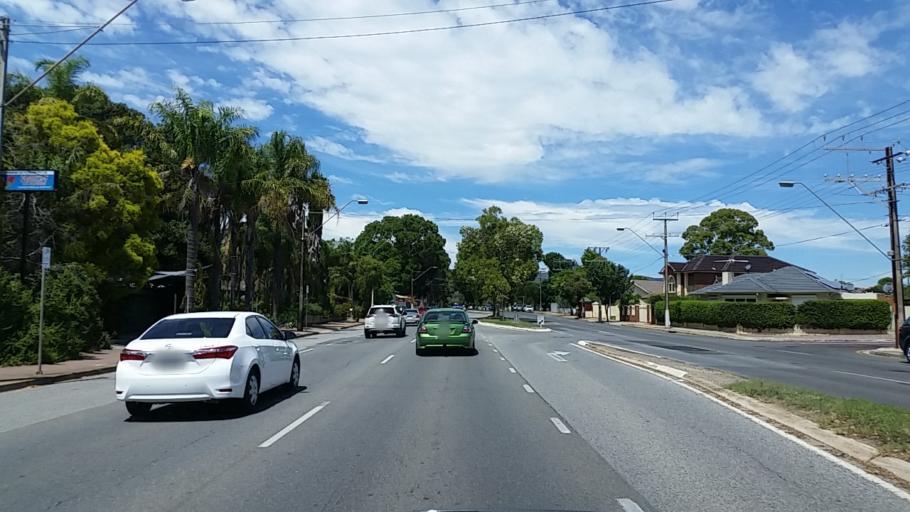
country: AU
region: South Australia
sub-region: Campbelltown
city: Paradise
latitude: -34.8696
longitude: 138.6654
